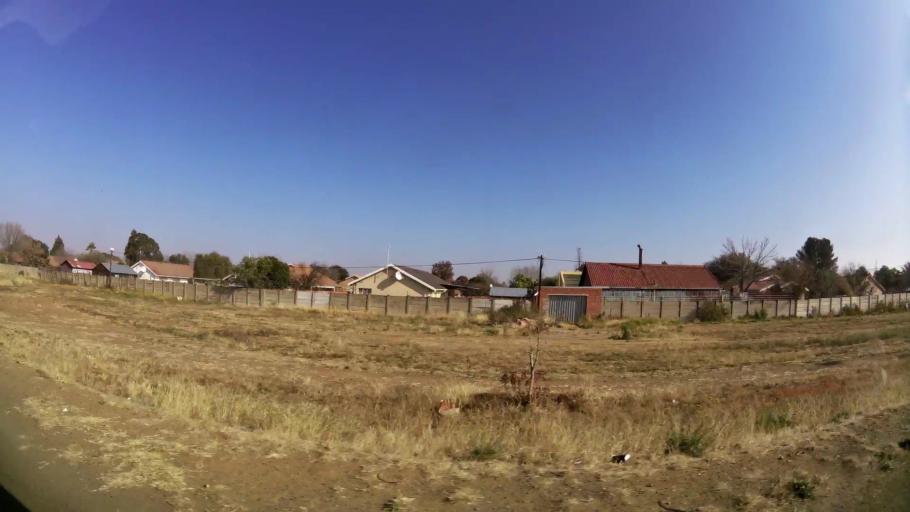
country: ZA
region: Orange Free State
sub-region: Mangaung Metropolitan Municipality
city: Bloemfontein
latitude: -29.1727
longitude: 26.1934
